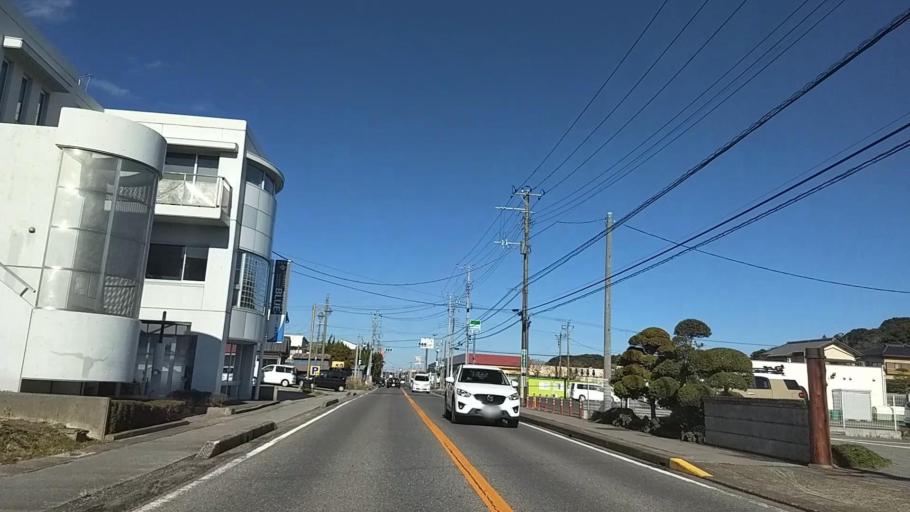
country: JP
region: Chiba
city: Ohara
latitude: 35.2394
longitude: 140.3913
